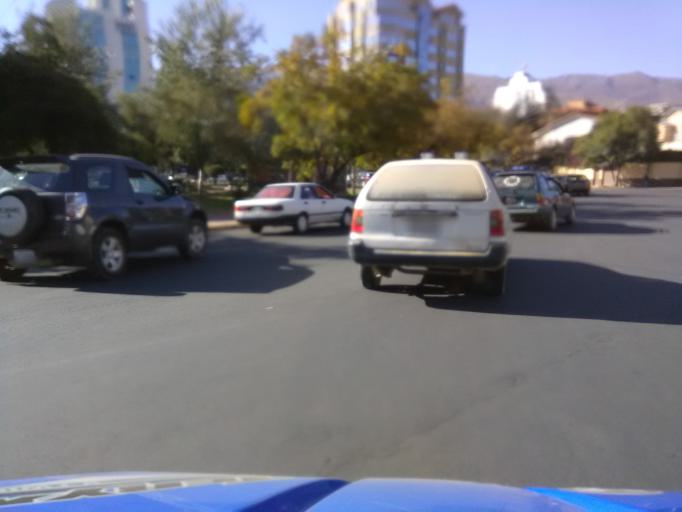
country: BO
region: Cochabamba
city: Cochabamba
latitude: -17.3827
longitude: -66.1516
